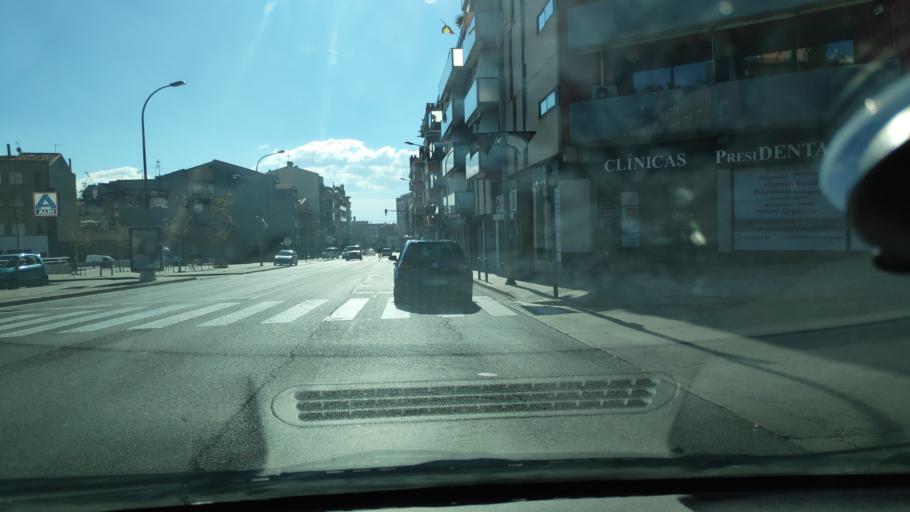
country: ES
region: Catalonia
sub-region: Provincia de Barcelona
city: Terrassa
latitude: 41.5777
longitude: 2.0175
